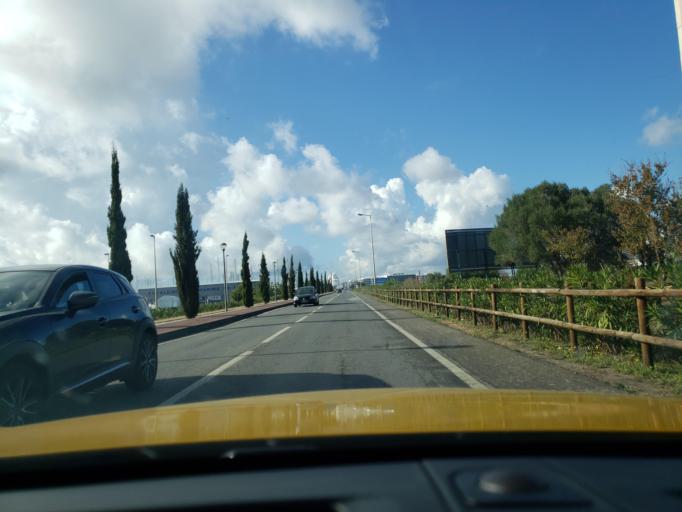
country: PT
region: Faro
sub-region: Portimao
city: Portimao
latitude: 37.1368
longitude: -8.5251
